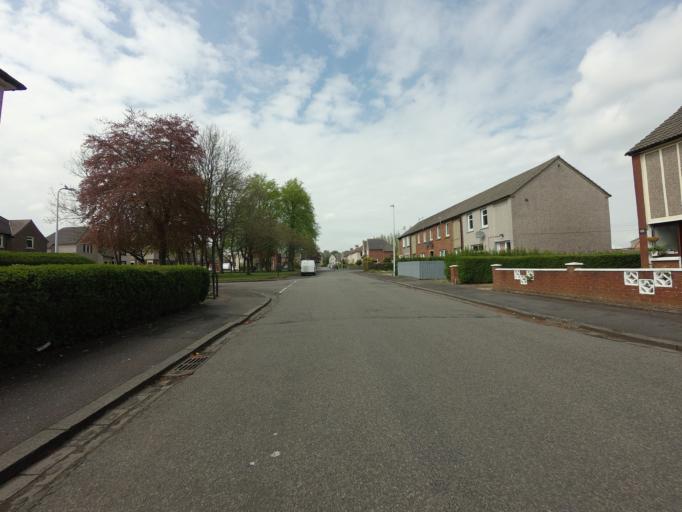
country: GB
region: Scotland
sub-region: Falkirk
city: Falkirk
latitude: 56.0034
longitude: -3.7658
